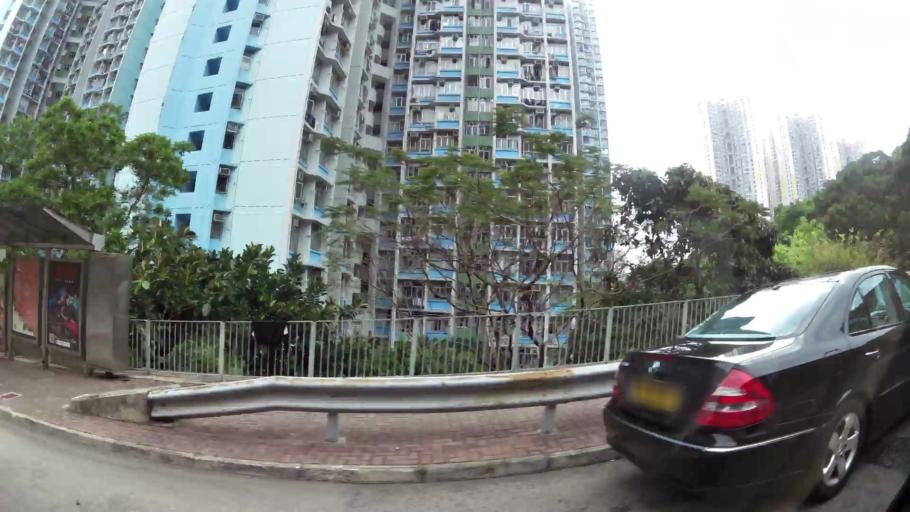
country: HK
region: Wanchai
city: Wan Chai
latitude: 22.2795
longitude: 114.2180
